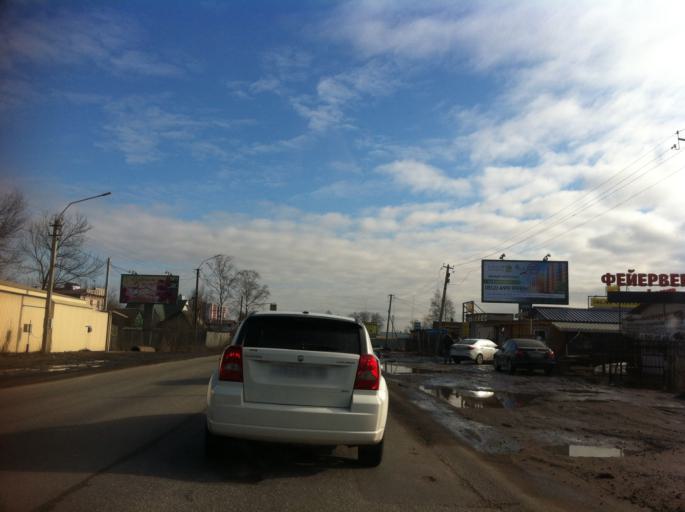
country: RU
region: Leningrad
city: Yanino Vtoroye
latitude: 59.9463
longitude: 30.5491
